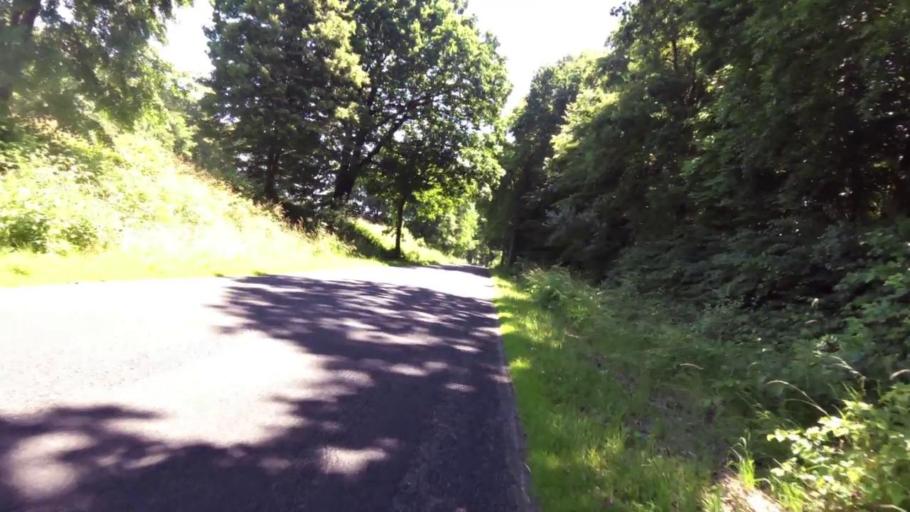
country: PL
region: West Pomeranian Voivodeship
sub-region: Powiat swidwinski
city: Rabino
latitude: 53.8467
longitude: 15.9918
